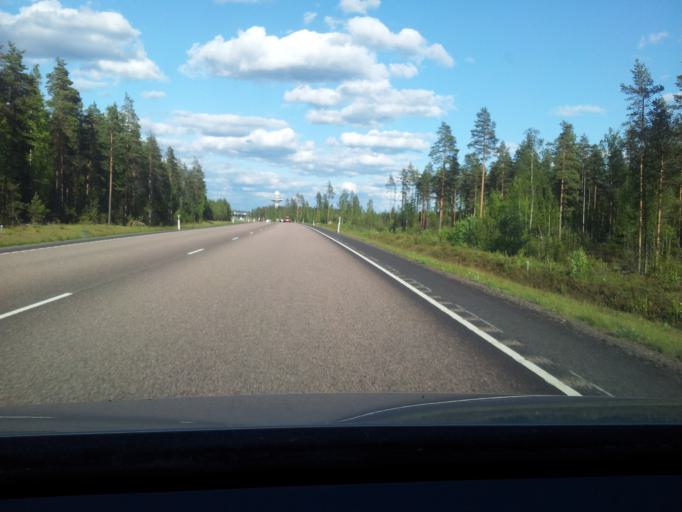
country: FI
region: Kymenlaakso
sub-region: Kouvola
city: Anjala
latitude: 60.9048
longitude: 27.0915
